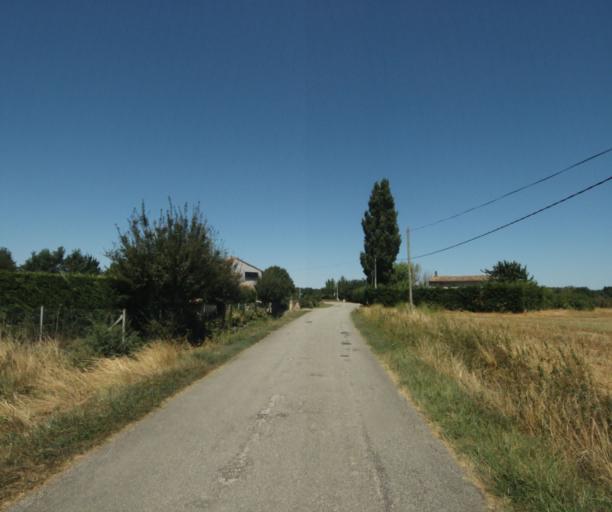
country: FR
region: Midi-Pyrenees
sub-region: Departement de la Haute-Garonne
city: Saint-Felix-Lauragais
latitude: 43.4500
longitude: 1.9374
